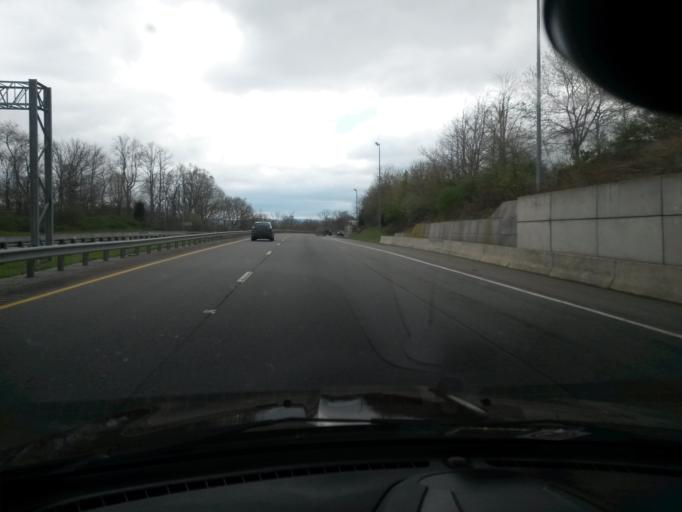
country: US
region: Virginia
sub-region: Montgomery County
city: Christiansburg
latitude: 37.1520
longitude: -80.4050
